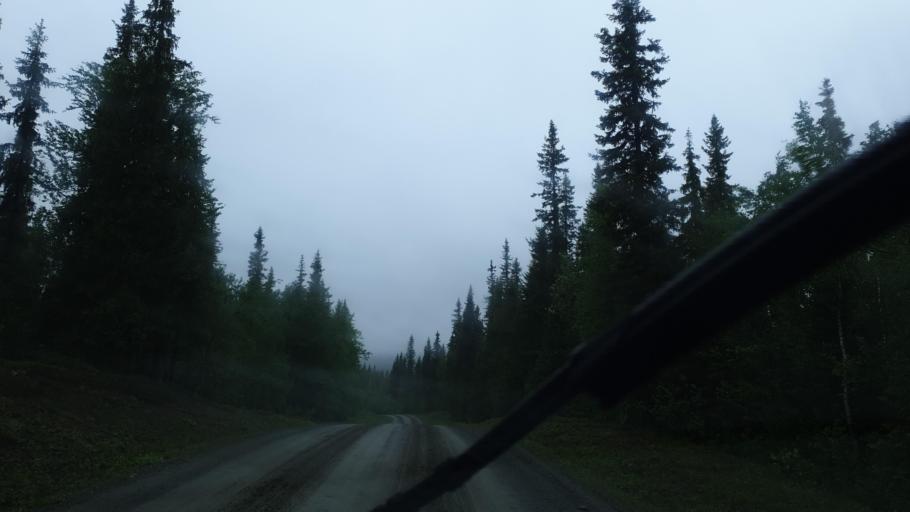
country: SE
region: Vaesterbotten
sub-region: Vilhelmina Kommun
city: Sjoberg
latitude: 65.2749
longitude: 15.9072
